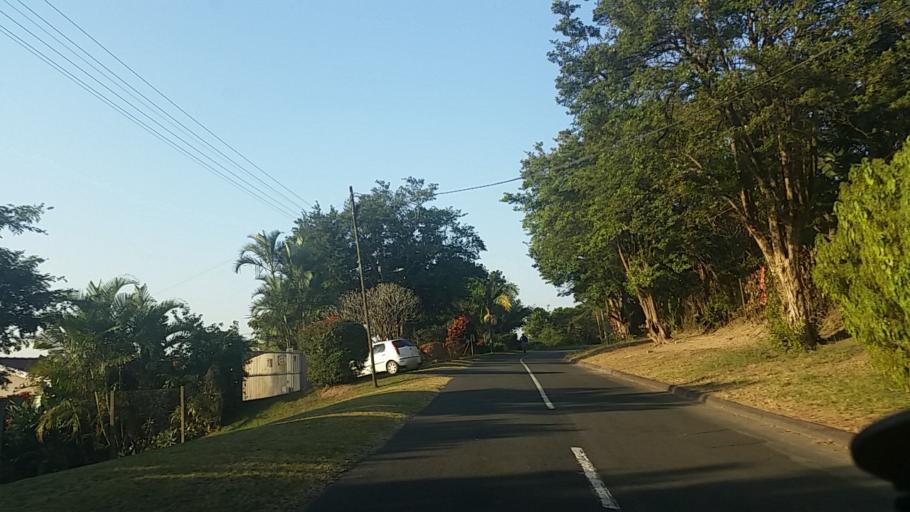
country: ZA
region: KwaZulu-Natal
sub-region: eThekwini Metropolitan Municipality
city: Berea
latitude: -29.8486
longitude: 30.9170
